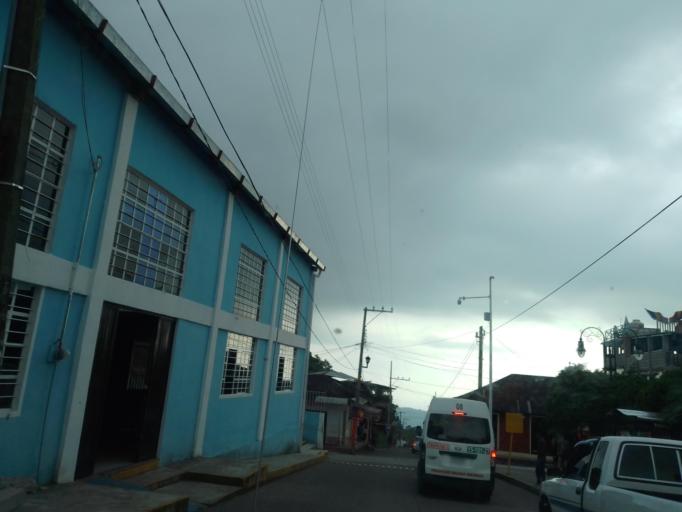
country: MX
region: Chiapas
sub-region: Union Juarez
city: Santo Domingo
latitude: 15.0603
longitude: -92.0816
